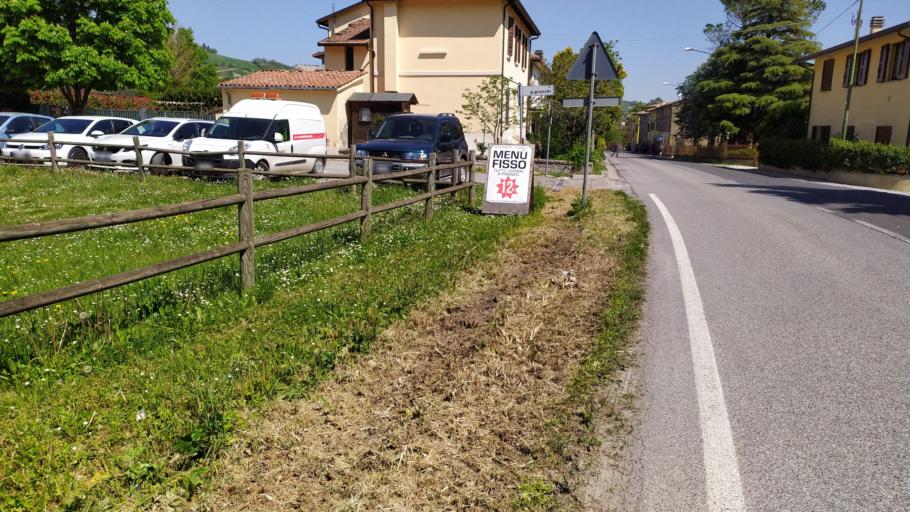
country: IT
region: Emilia-Romagna
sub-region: Provincia di Ravenna
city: Casola Valsenio
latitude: 44.2598
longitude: 11.6706
